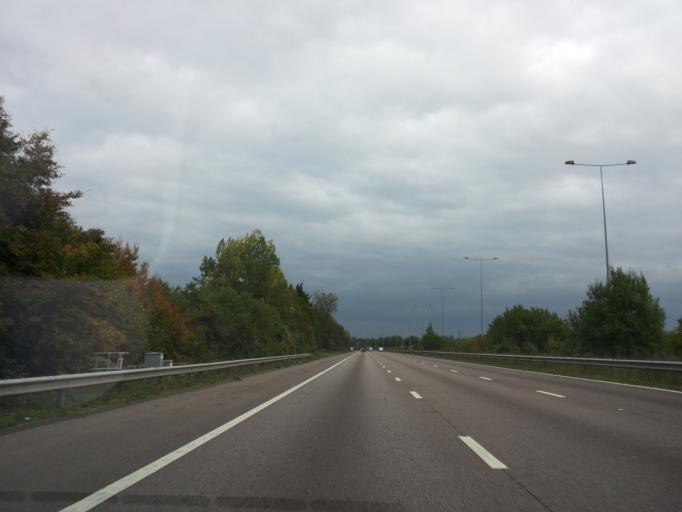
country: GB
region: England
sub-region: Kent
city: Boxley
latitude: 51.3254
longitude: 0.5445
